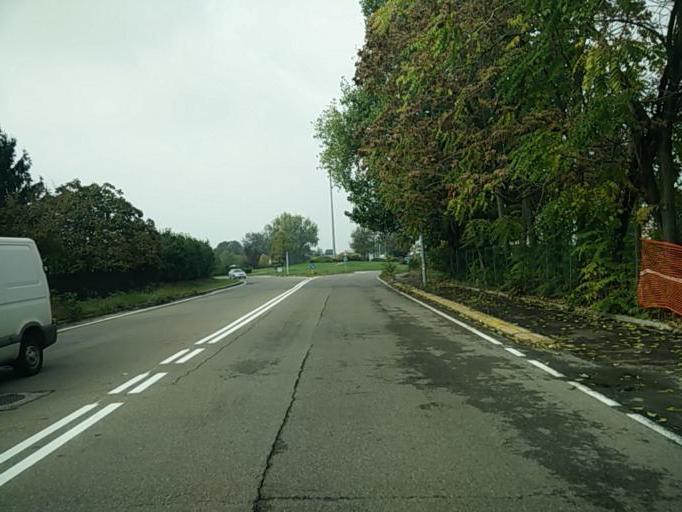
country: IT
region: Emilia-Romagna
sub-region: Provincia di Modena
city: Carpi Centro
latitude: 44.7827
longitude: 10.8616
